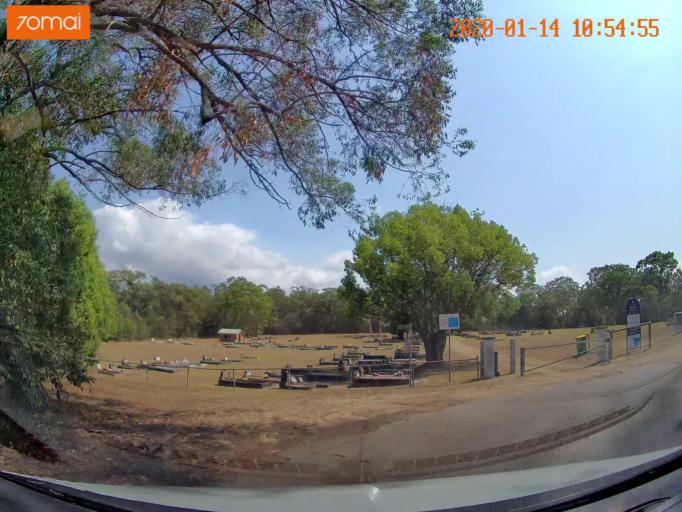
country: AU
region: New South Wales
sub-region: Lake Macquarie Shire
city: Dora Creek
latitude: -33.0969
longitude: 151.4858
